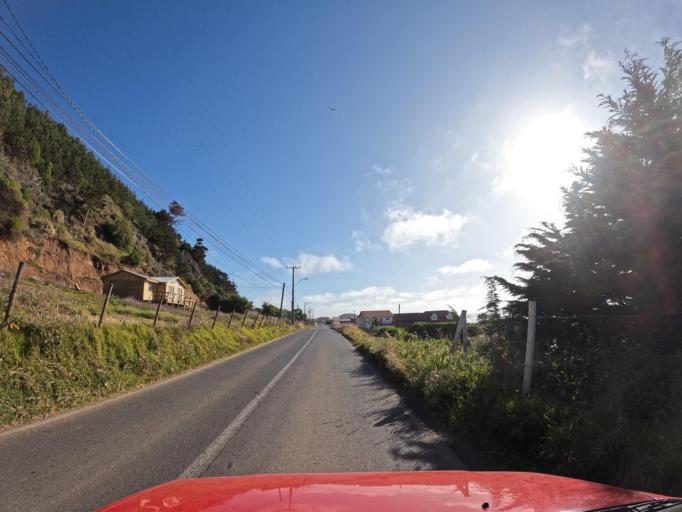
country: CL
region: Maule
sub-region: Provincia de Talca
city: Constitucion
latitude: -34.8919
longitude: -72.1756
